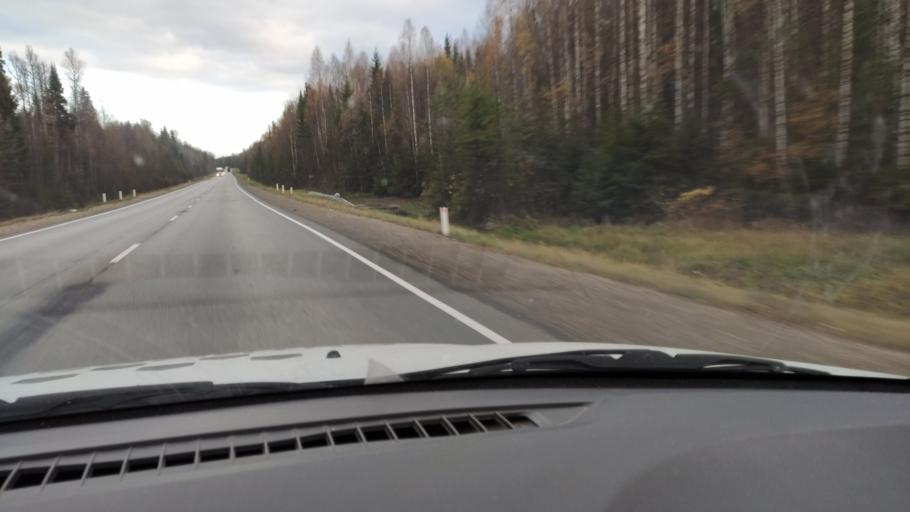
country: RU
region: Kirov
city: Chernaya Kholunitsa
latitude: 58.8403
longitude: 51.7511
